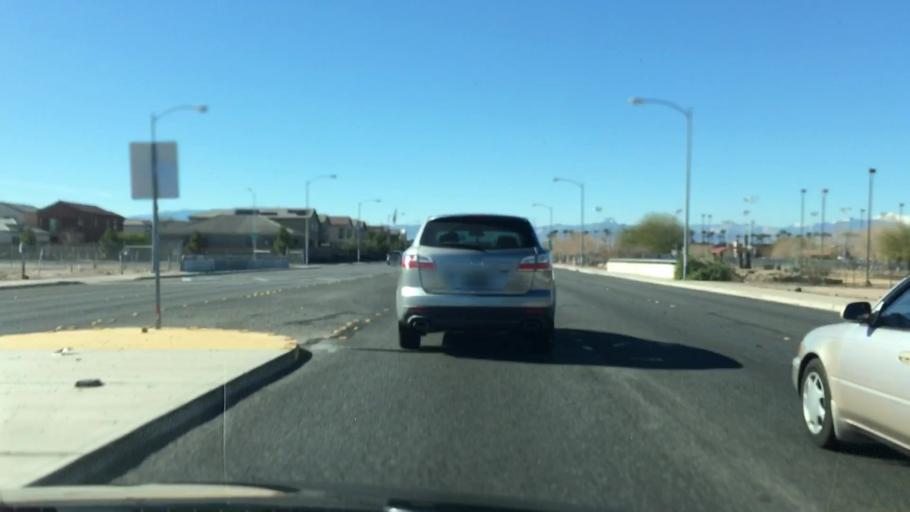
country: US
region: Nevada
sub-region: Clark County
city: Whitney
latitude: 36.0570
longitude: -115.1127
